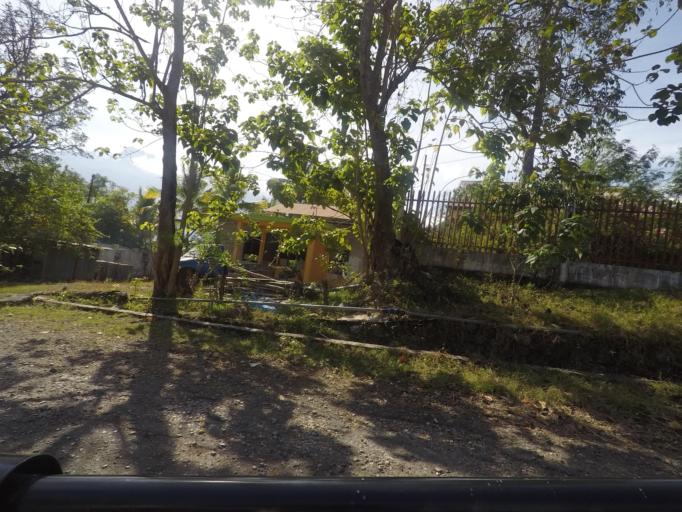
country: TL
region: Bobonaro
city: Maliana
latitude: -8.9977
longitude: 125.2254
